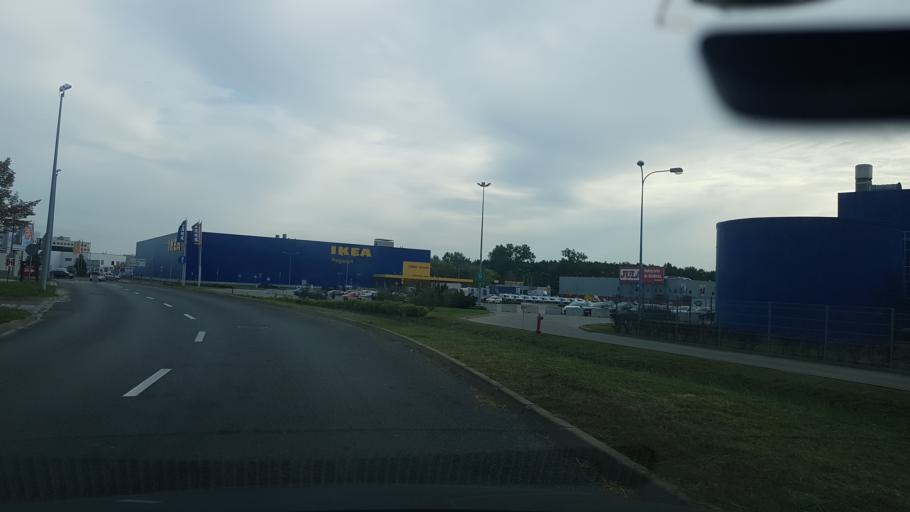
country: PL
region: Masovian Voivodeship
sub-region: Powiat wolominski
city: Zabki
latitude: 52.3058
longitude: 21.0846
